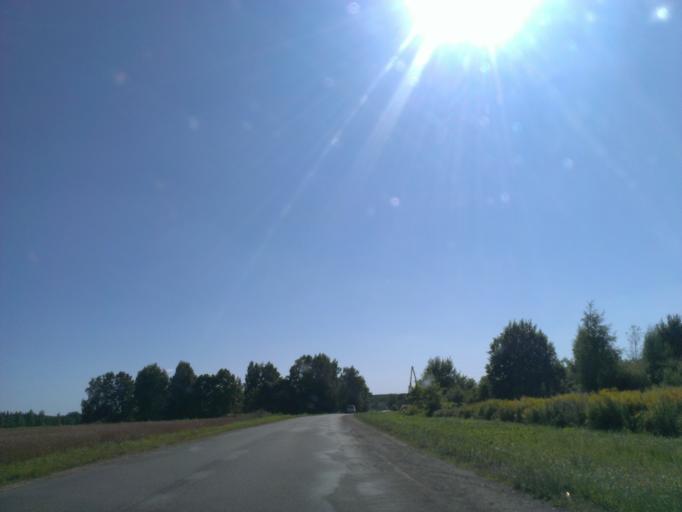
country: LV
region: Sigulda
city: Sigulda
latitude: 57.1372
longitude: 24.8421
